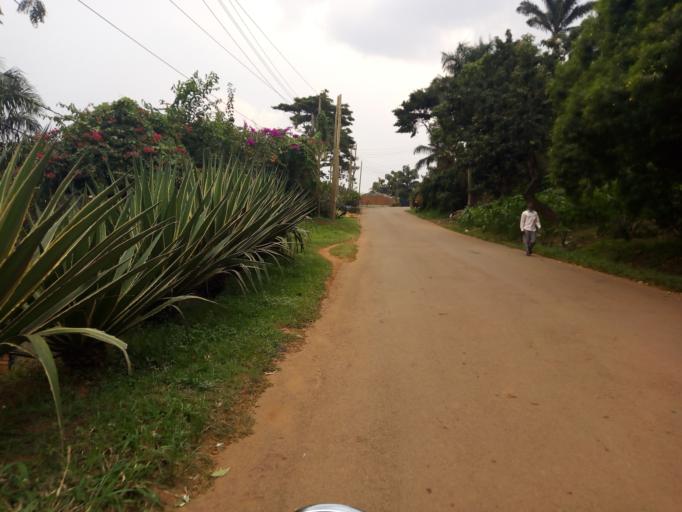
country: UG
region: Central Region
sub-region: Wakiso District
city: Kireka
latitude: 0.3265
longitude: 32.6262
